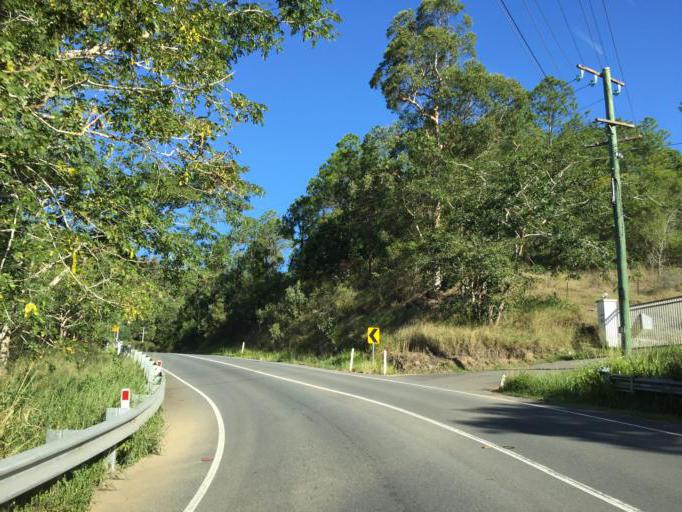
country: AU
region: Queensland
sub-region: Brisbane
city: Kenmore Hills
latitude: -27.4568
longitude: 152.9300
